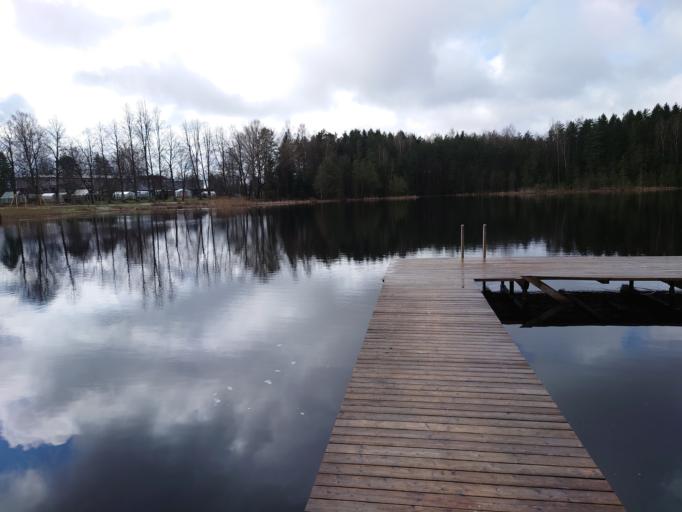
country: EE
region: Vorumaa
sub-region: Voru linn
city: Voru
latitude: 57.9102
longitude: 26.9831
